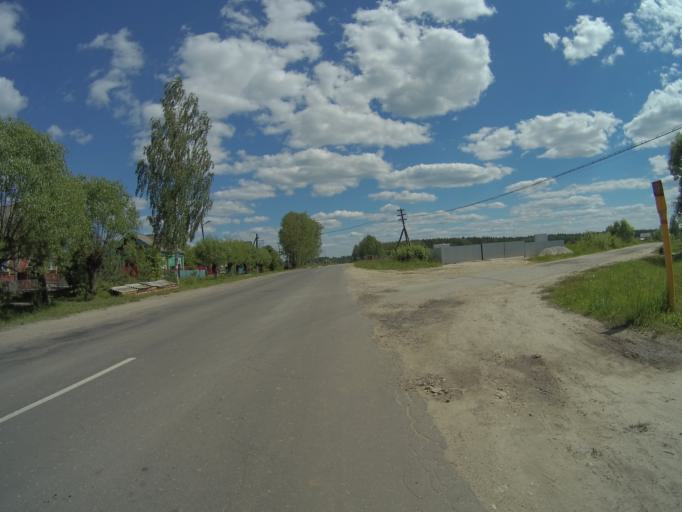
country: RU
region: Vladimir
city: Sudogda
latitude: 56.0688
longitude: 40.7976
